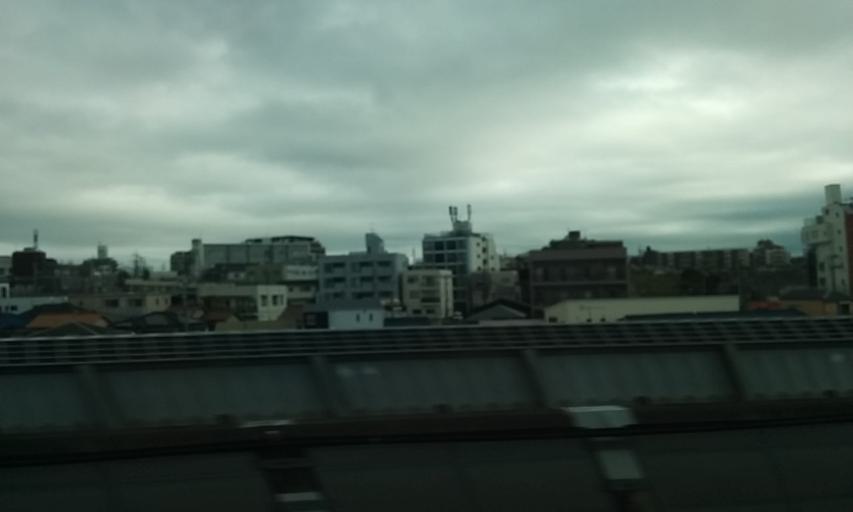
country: JP
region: Hyogo
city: Akashi
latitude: 34.6969
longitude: 134.9037
